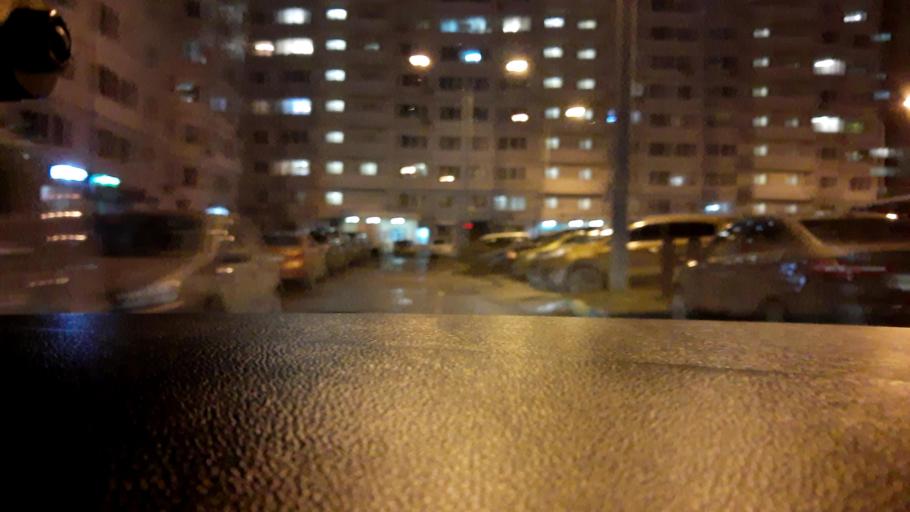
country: RU
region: Moskovskaya
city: Nemchinovka
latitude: 55.7069
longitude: 37.3274
